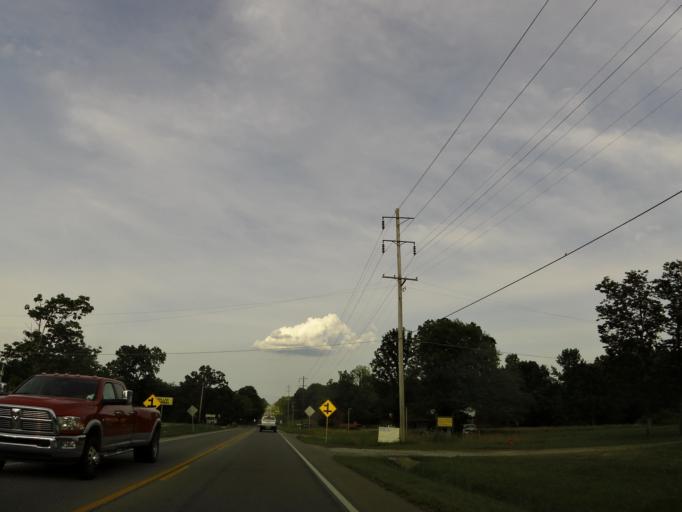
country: US
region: Tennessee
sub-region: Humphreys County
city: McEwen
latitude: 36.0913
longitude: -87.5193
